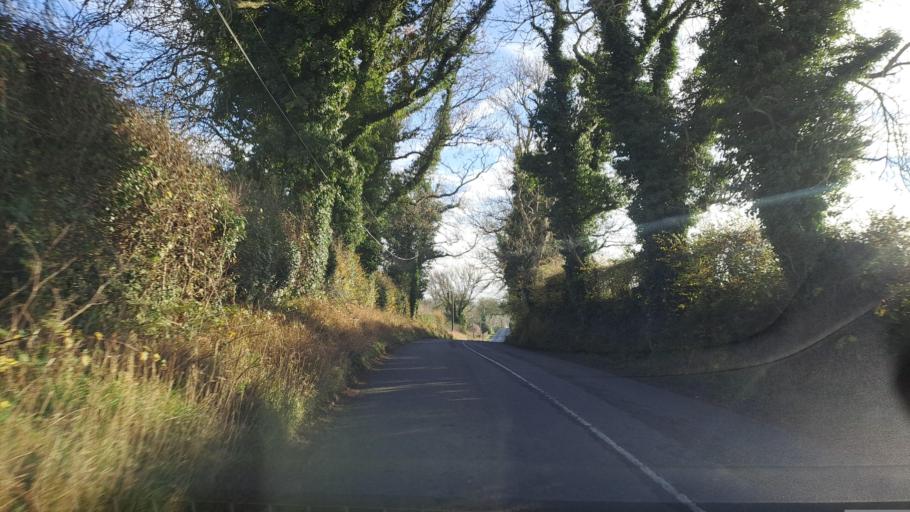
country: IE
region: Leinster
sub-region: Lu
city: Ardee
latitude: 53.8553
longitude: -6.6654
